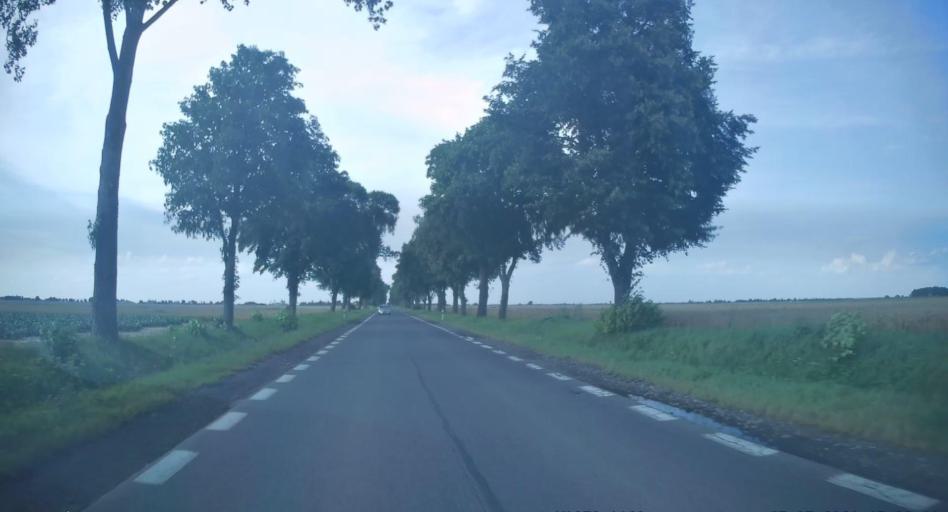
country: PL
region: Lodz Voivodeship
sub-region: Powiat tomaszowski
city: Rzeczyca
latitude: 51.6171
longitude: 20.2931
